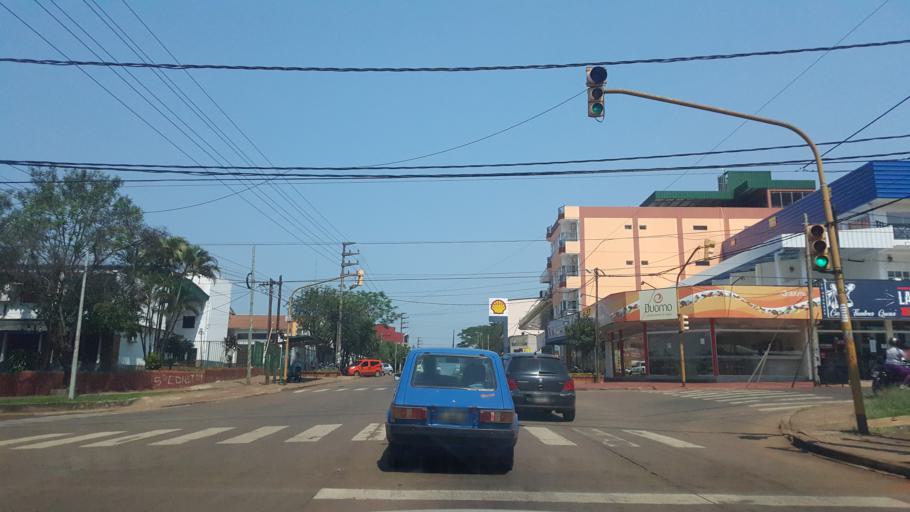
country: AR
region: Misiones
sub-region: Departamento de Capital
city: Posadas
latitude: -27.3895
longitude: -55.9121
